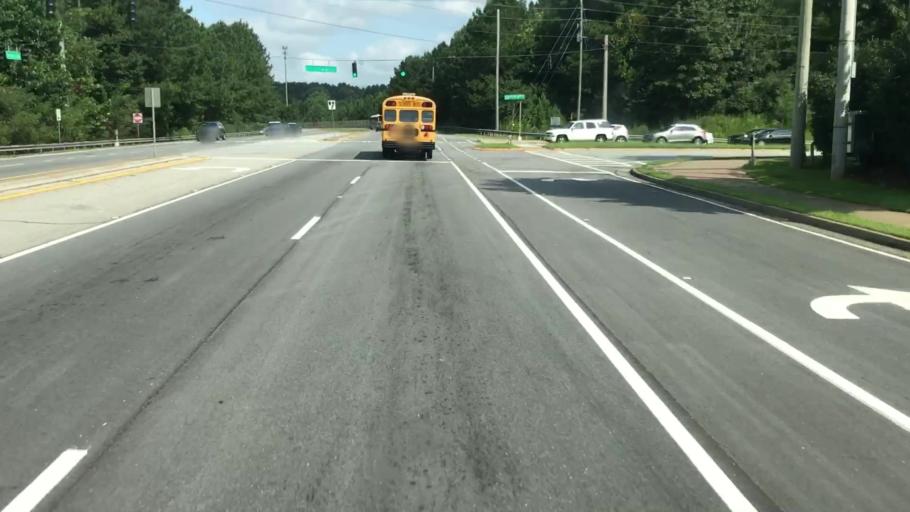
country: US
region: Georgia
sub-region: Gwinnett County
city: Lawrenceville
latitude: 33.9344
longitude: -84.0293
